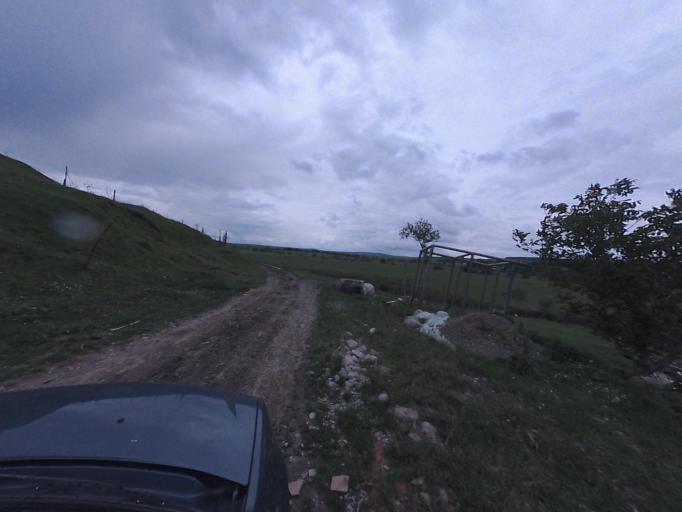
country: RO
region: Neamt
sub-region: Comuna Dulcesti
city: Dulcesti
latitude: 46.9639
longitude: 26.7805
